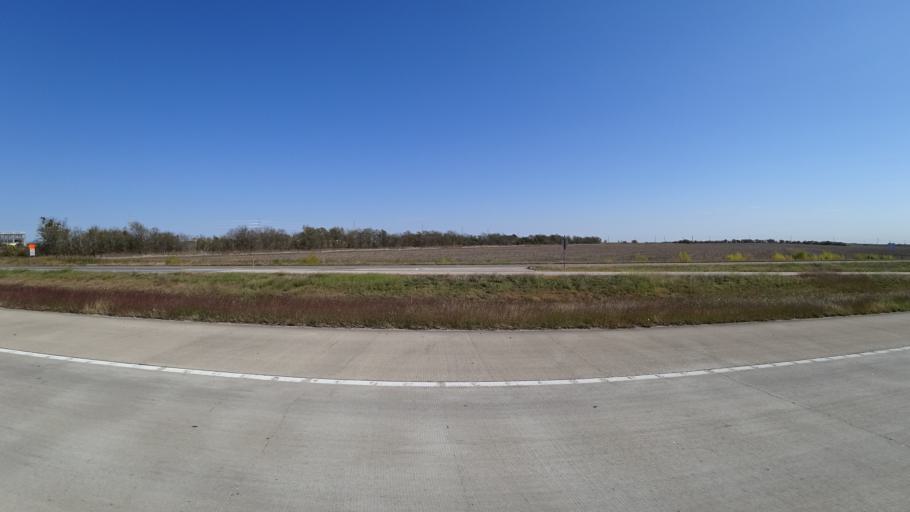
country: US
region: Texas
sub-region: Travis County
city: Pflugerville
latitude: 30.4465
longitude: -97.5937
